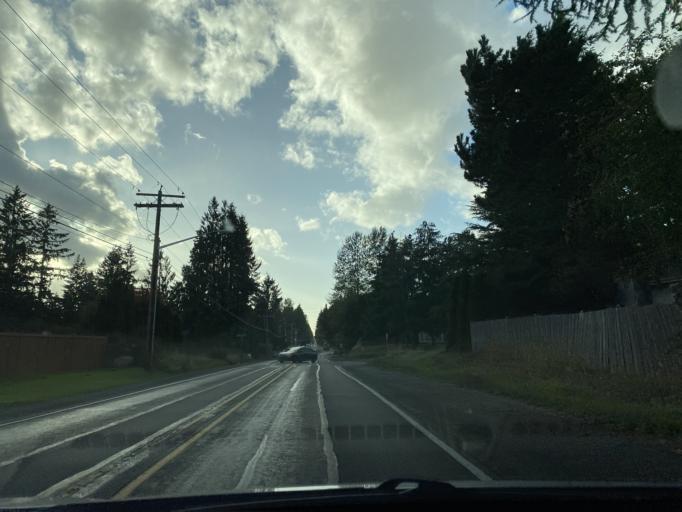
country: US
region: Washington
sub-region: Pierce County
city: South Hill
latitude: 47.1184
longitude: -122.2891
